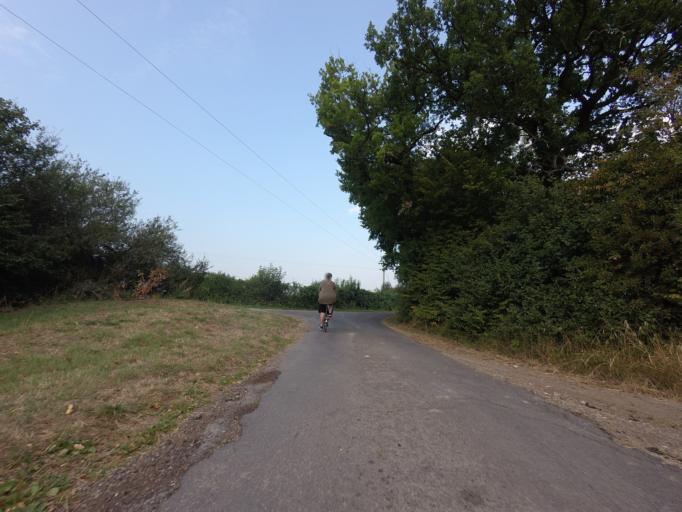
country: GB
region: England
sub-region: Kent
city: Tenterden
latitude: 51.1131
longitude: 0.7751
